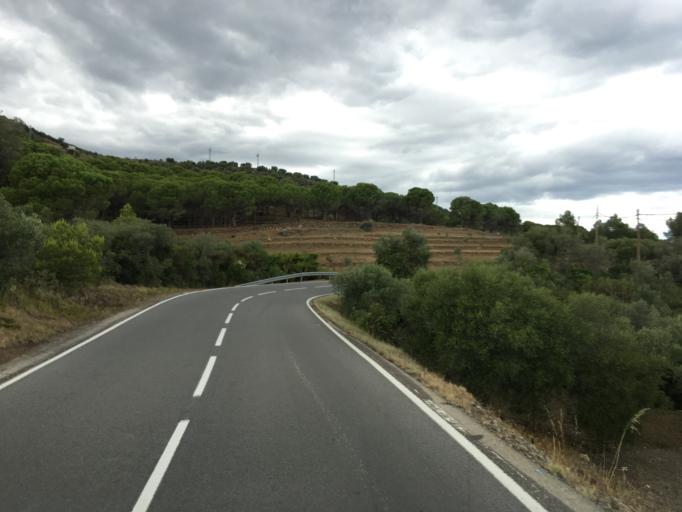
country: ES
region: Catalonia
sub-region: Provincia de Girona
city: Llanca
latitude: 42.3448
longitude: 3.1830
